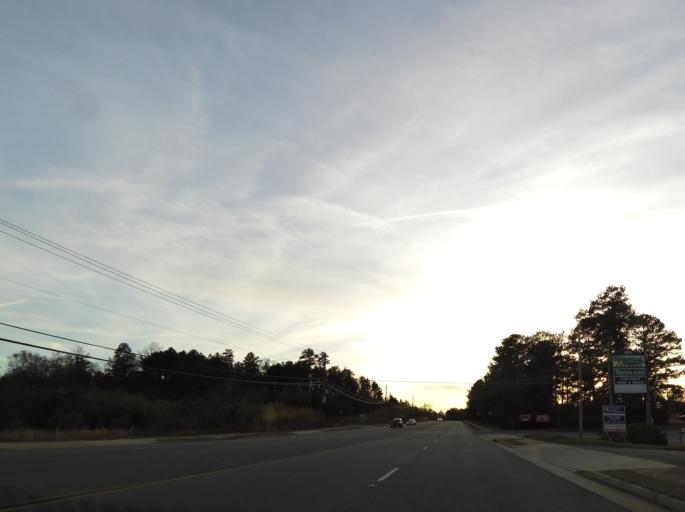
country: US
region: Georgia
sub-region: Bibb County
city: Macon
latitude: 32.7557
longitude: -83.6635
